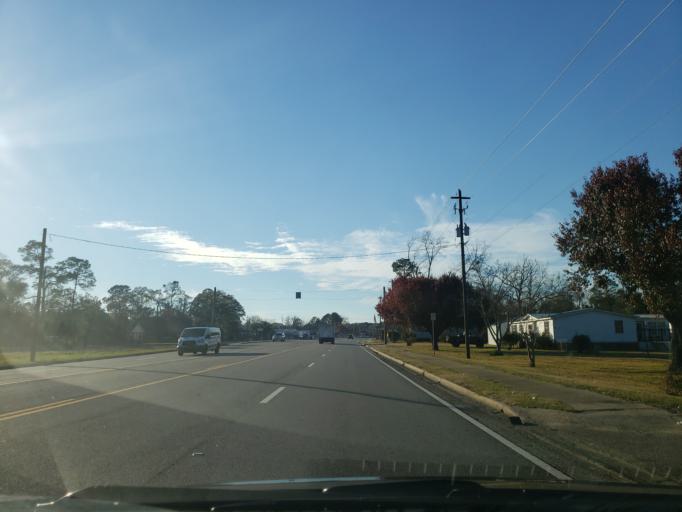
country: US
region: Georgia
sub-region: Atkinson County
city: Pearson
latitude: 31.2973
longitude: -82.8484
